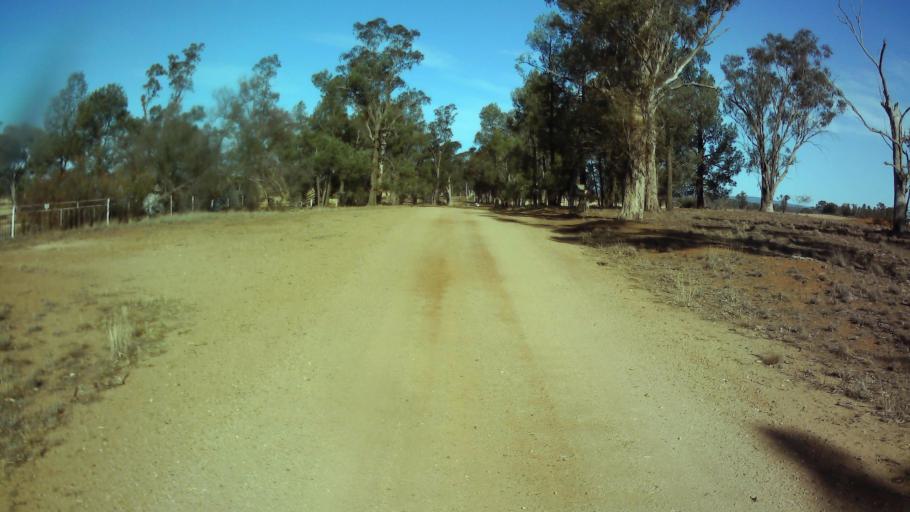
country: AU
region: New South Wales
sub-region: Weddin
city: Grenfell
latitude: -33.6607
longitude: 148.1199
